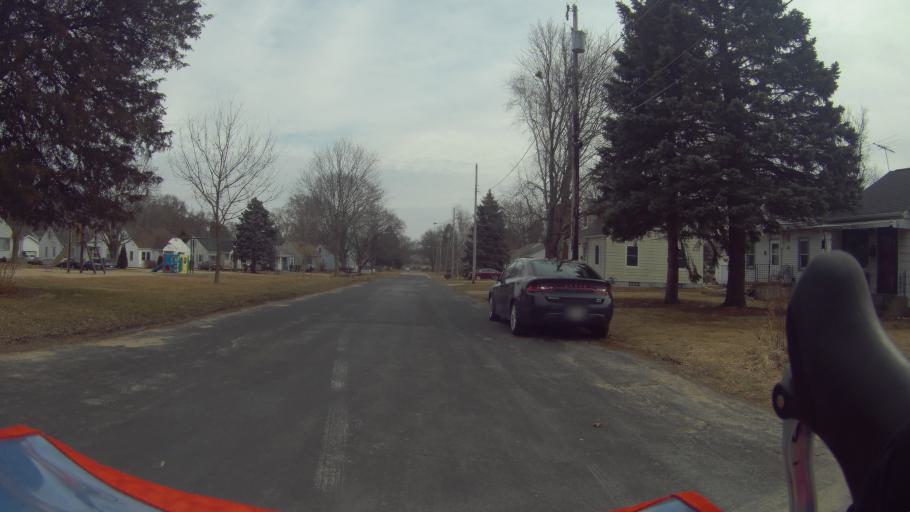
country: US
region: Wisconsin
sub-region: Dane County
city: Maple Bluff
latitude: 43.1177
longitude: -89.3677
